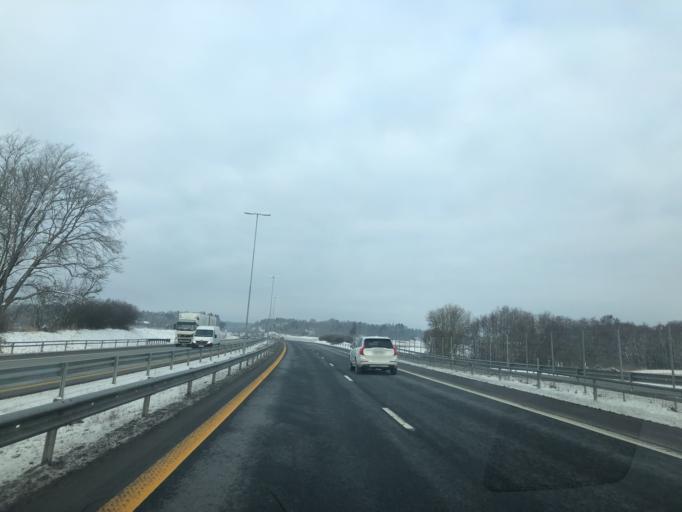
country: NO
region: Ostfold
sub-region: Sarpsborg
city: Skjeberg
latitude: 59.1466
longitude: 11.2494
